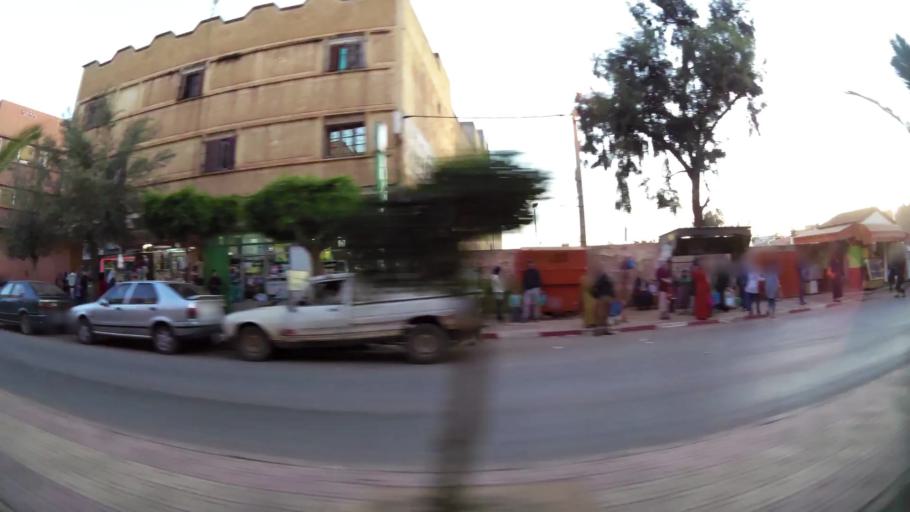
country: MA
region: Oriental
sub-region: Berkane-Taourirt
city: Berkane
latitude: 34.9207
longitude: -2.3219
